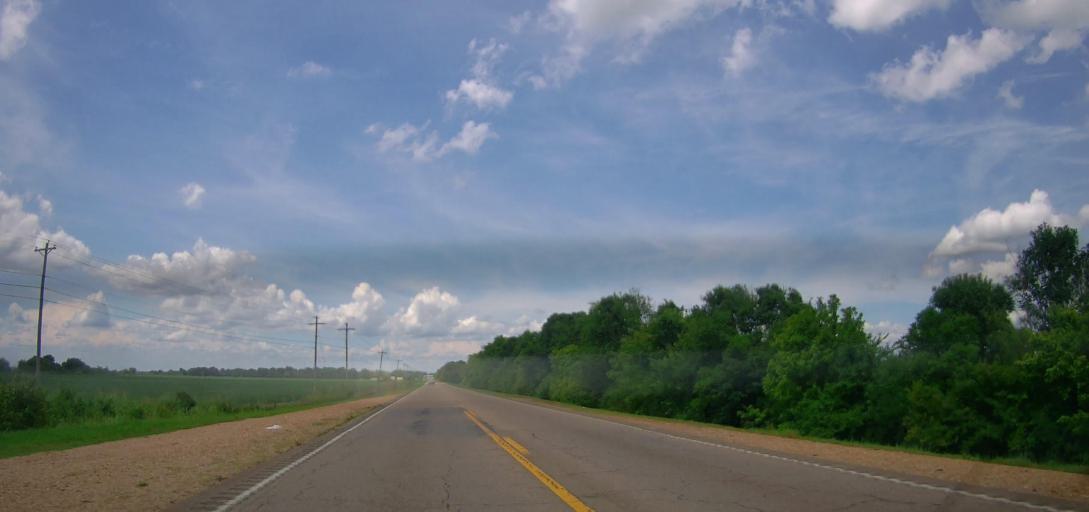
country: US
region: Mississippi
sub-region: Lee County
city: Shannon
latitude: 34.1402
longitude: -88.7194
